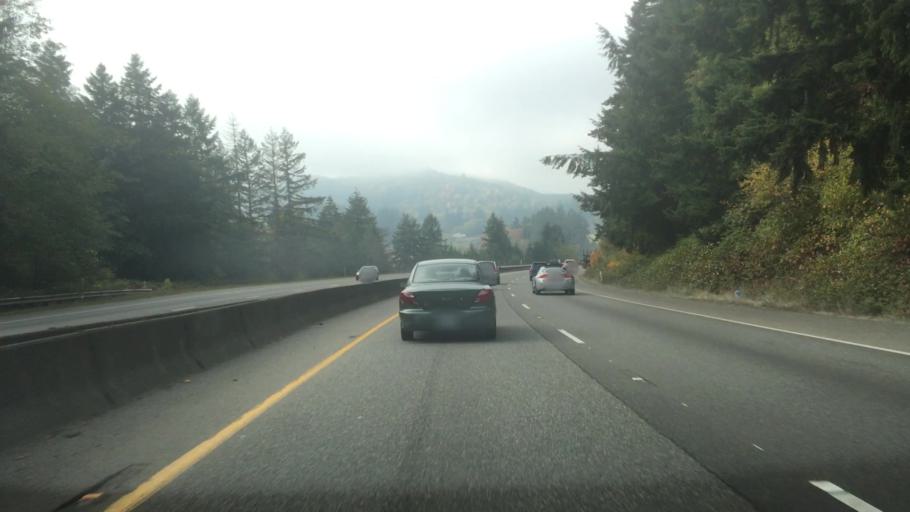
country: US
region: Washington
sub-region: Thurston County
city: Tumwater
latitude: 47.0422
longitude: -122.9824
